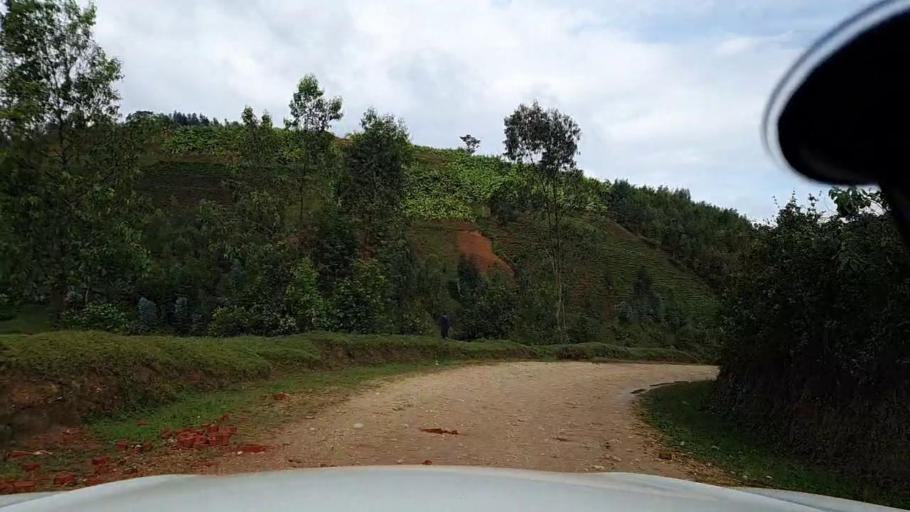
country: RW
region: Western Province
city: Kibuye
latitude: -2.1208
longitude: 29.4943
